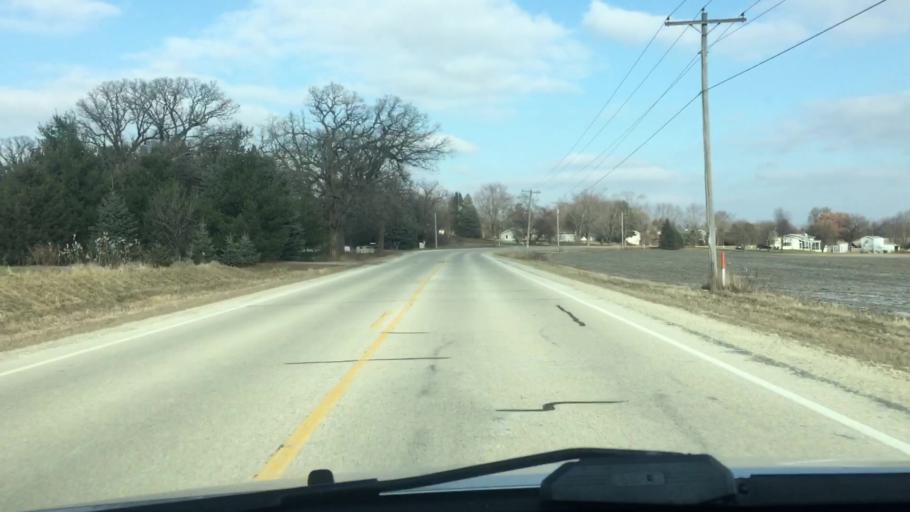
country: US
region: Wisconsin
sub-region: Jefferson County
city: Palmyra
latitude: 42.8989
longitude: -88.5510
